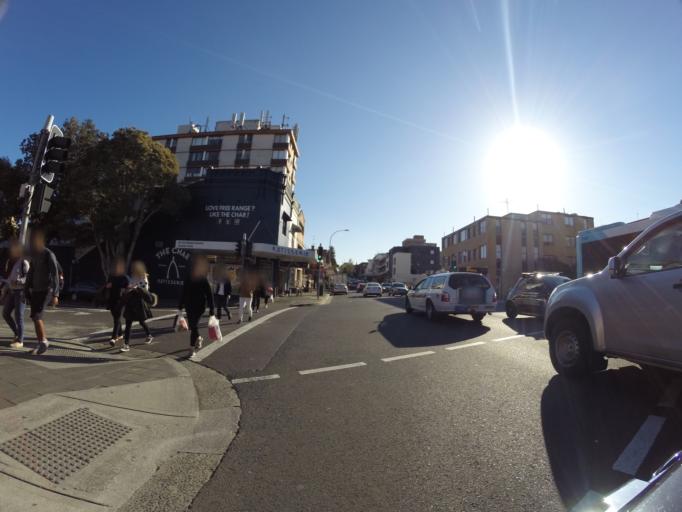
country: AU
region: New South Wales
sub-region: Waverley
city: Bondi
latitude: -33.8938
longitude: 151.2626
